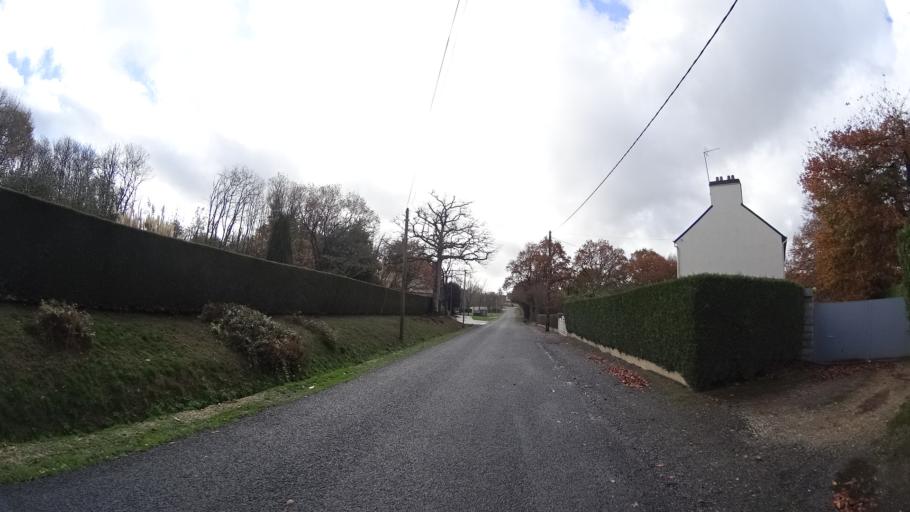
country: FR
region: Pays de la Loire
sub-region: Departement de la Loire-Atlantique
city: Fegreac
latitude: 47.6010
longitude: -2.0663
